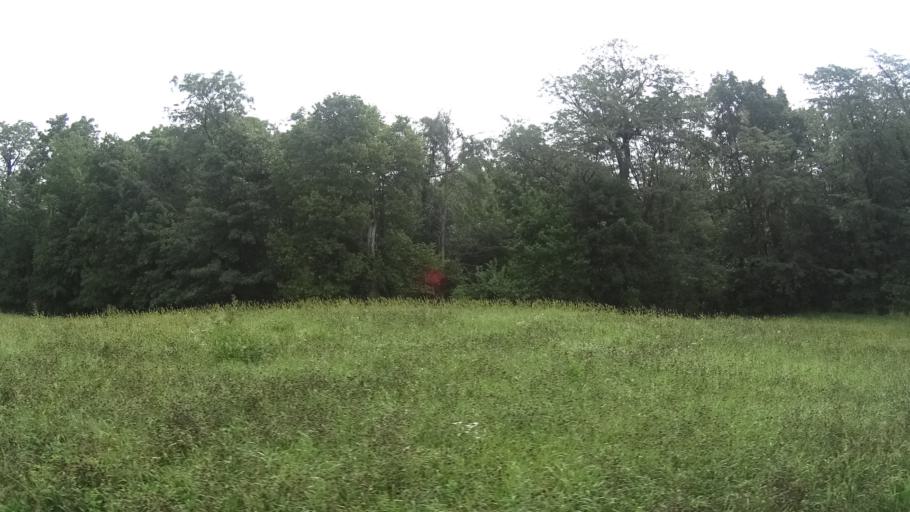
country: US
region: Indiana
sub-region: Madison County
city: Pendleton
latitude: 40.0147
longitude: -85.7912
